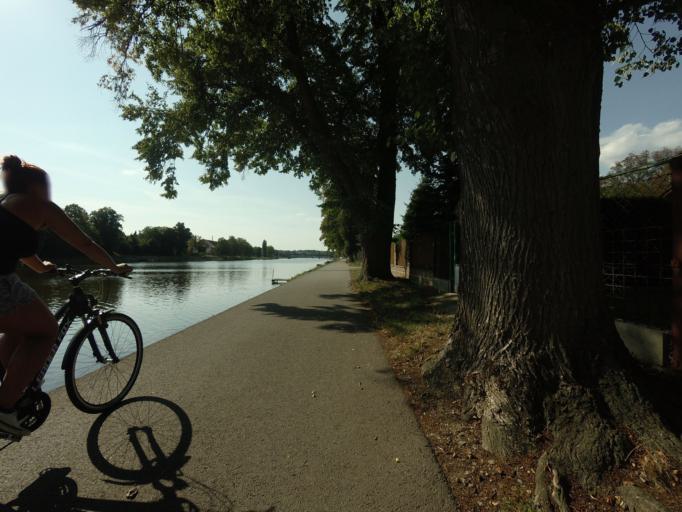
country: CZ
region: Jihocesky
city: Tyn nad Vltavou
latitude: 49.2188
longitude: 14.4279
